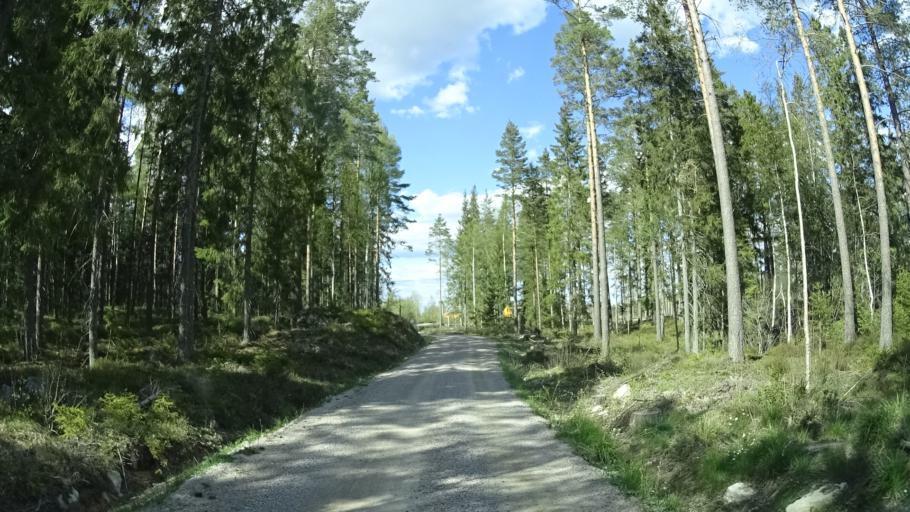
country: SE
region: OErebro
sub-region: Orebro Kommun
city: Garphyttan
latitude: 59.4224
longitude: 14.8654
